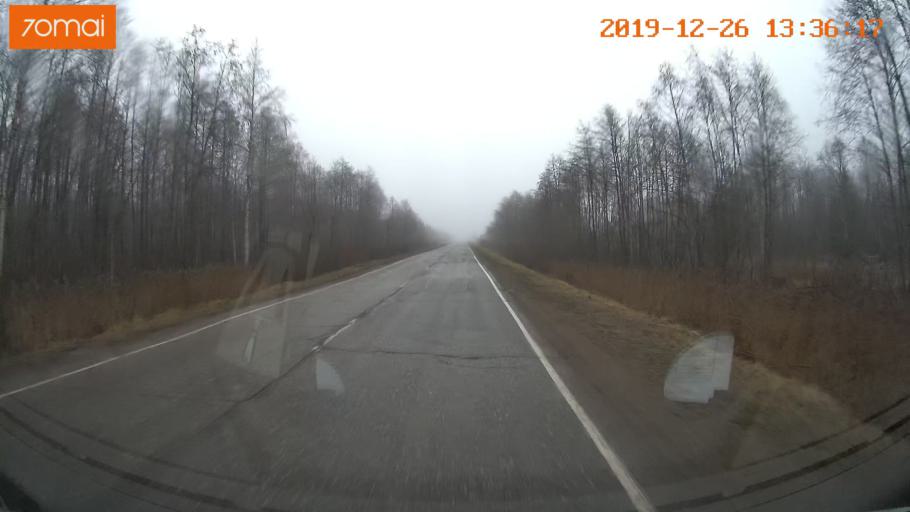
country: RU
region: Vologda
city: Sheksna
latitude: 58.7842
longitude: 38.3529
